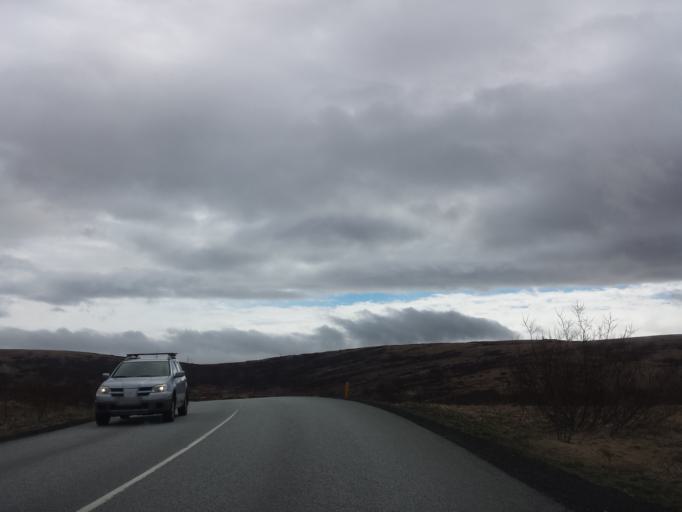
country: IS
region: Capital Region
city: Gardabaer
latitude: 64.0824
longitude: -21.8812
